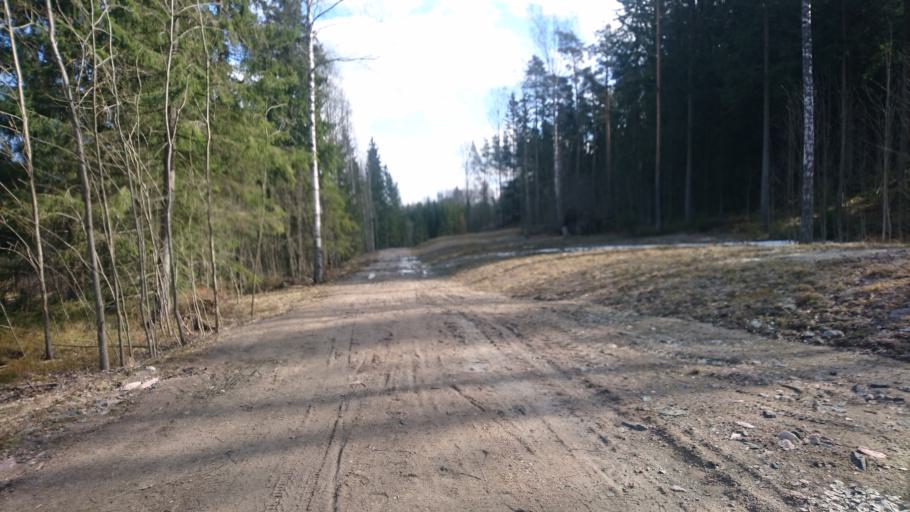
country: FI
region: Uusimaa
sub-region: Helsinki
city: Kauniainen
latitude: 60.2001
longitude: 24.7292
